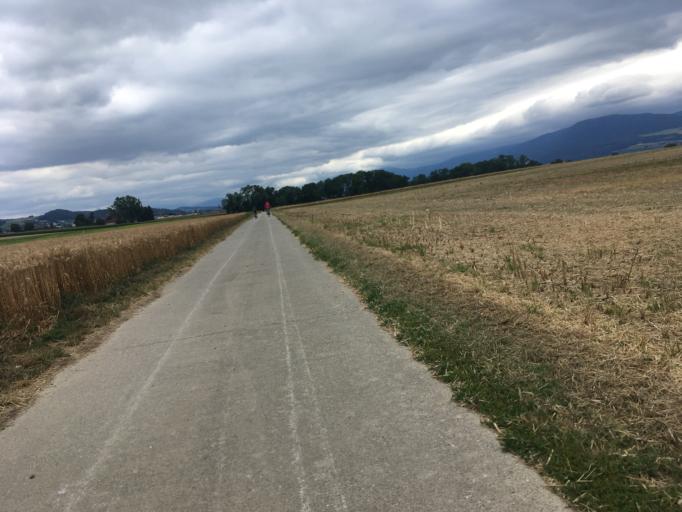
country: CH
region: Fribourg
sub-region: Broye District
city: Estavayer-le-Lac
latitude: 46.8597
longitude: 6.8711
